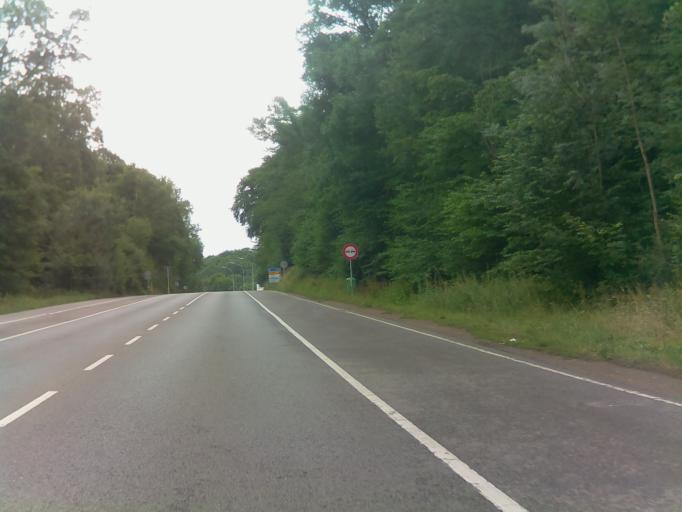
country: LU
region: Luxembourg
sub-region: Canton d'Esch-sur-Alzette
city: Bettembourg
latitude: 49.5080
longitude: 6.1219
